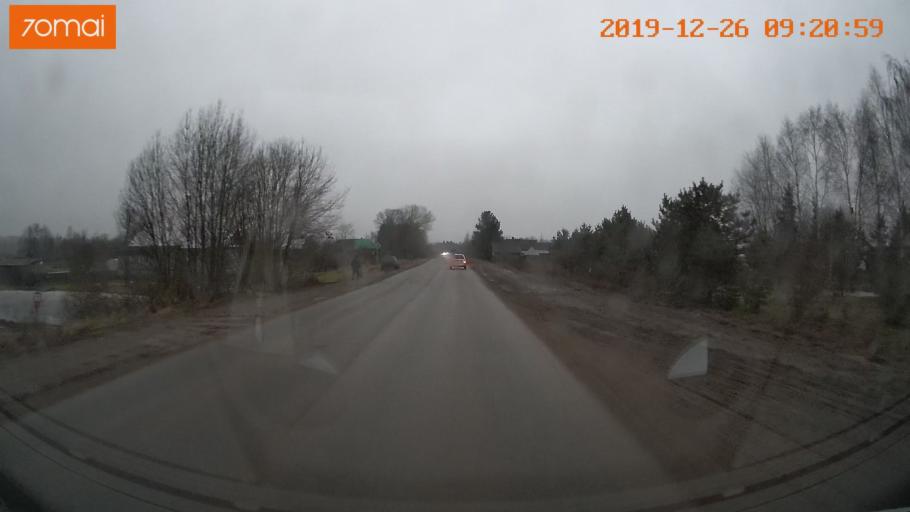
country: RU
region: Vologda
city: Gryazovets
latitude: 58.9664
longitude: 40.2269
